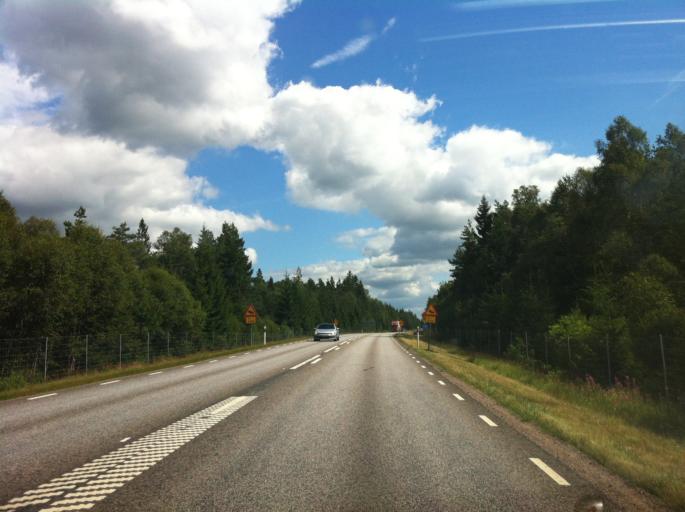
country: SE
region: Halland
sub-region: Hylte Kommun
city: Hyltebruk
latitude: 57.0521
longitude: 13.3252
